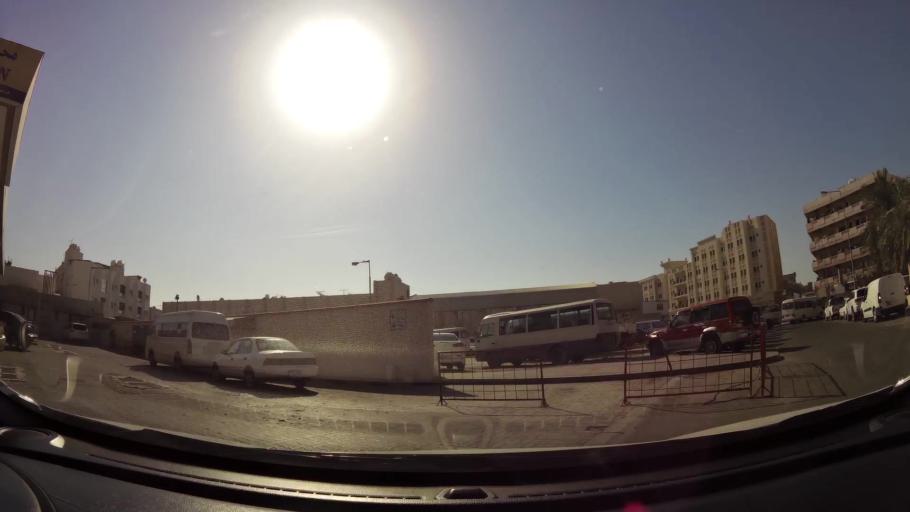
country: BH
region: Manama
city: Manama
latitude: 26.2273
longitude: 50.5820
